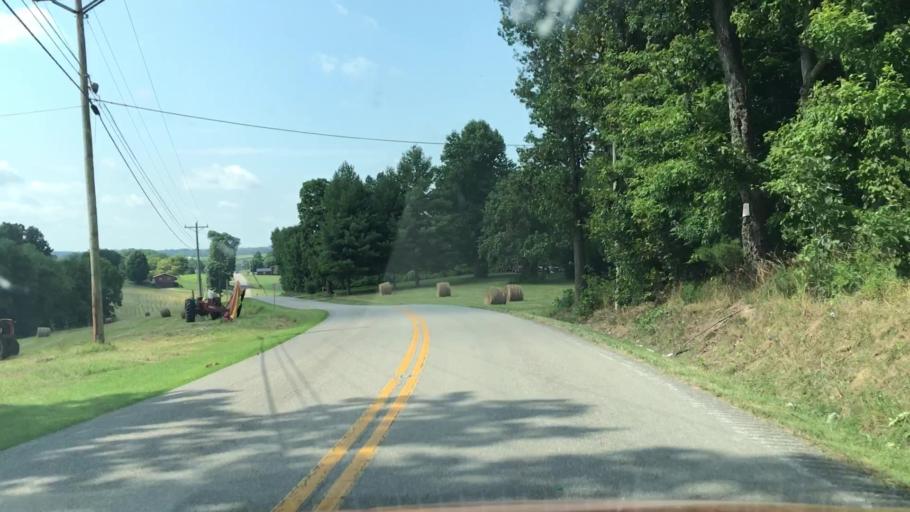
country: US
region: Kentucky
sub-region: Barren County
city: Glasgow
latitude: 36.8807
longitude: -85.8477
